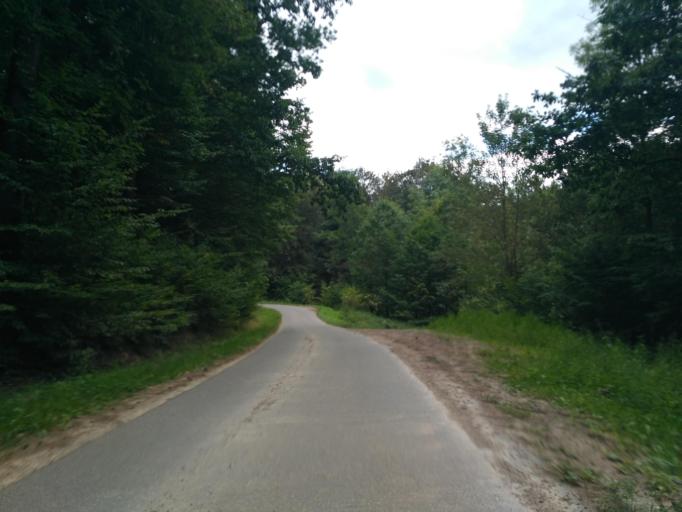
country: PL
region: Subcarpathian Voivodeship
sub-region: Powiat rzeszowski
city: Dynow
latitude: 49.7608
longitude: 22.2799
